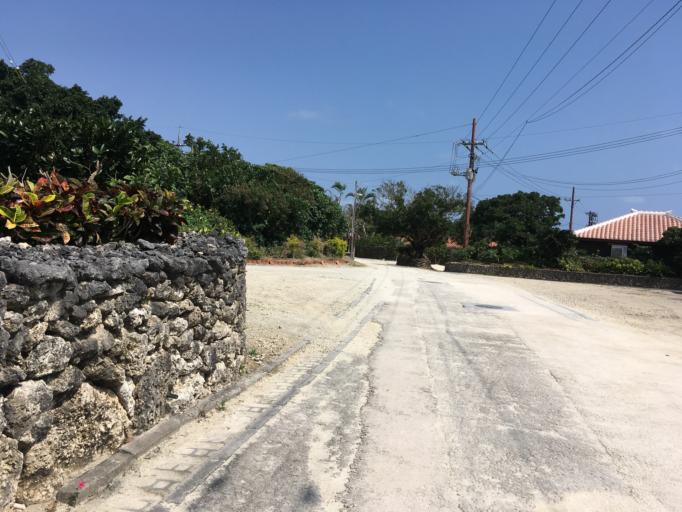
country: JP
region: Okinawa
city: Ishigaki
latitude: 24.3311
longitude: 124.0824
